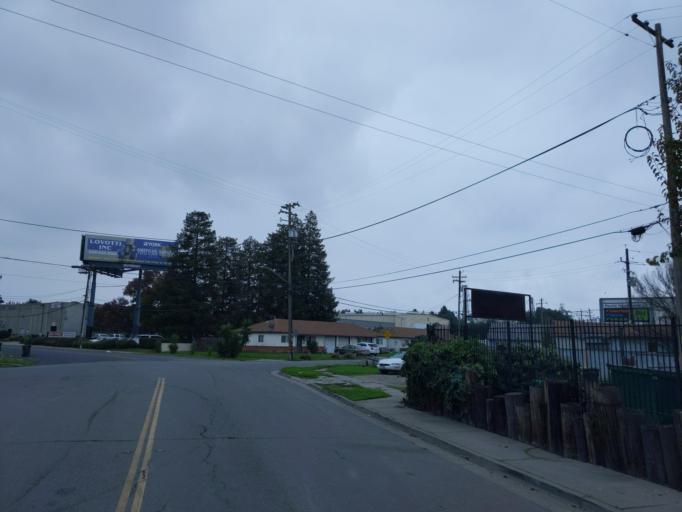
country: US
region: California
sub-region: San Joaquin County
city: Country Club
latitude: 37.9556
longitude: -121.3252
